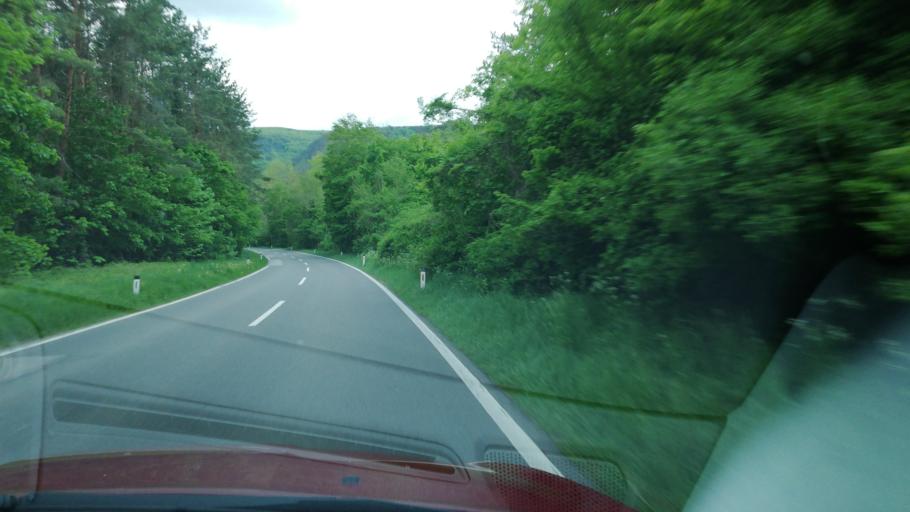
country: AT
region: Lower Austria
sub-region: Politischer Bezirk Modling
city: Gaaden
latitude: 48.0173
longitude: 16.1765
